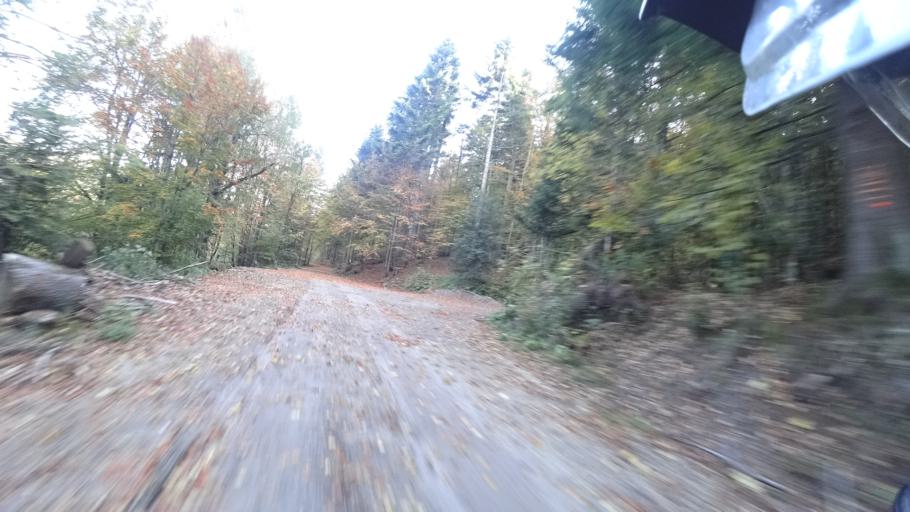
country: HR
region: Karlovacka
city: Plaski
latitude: 44.9410
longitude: 15.4565
